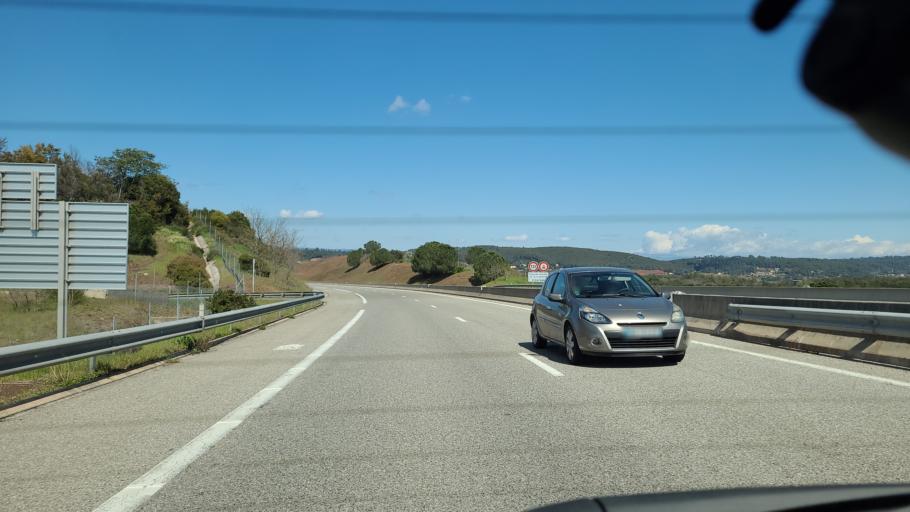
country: FR
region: Provence-Alpes-Cote d'Azur
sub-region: Departement du Var
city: Le Cannet-des-Maures
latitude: 43.3825
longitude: 6.3588
